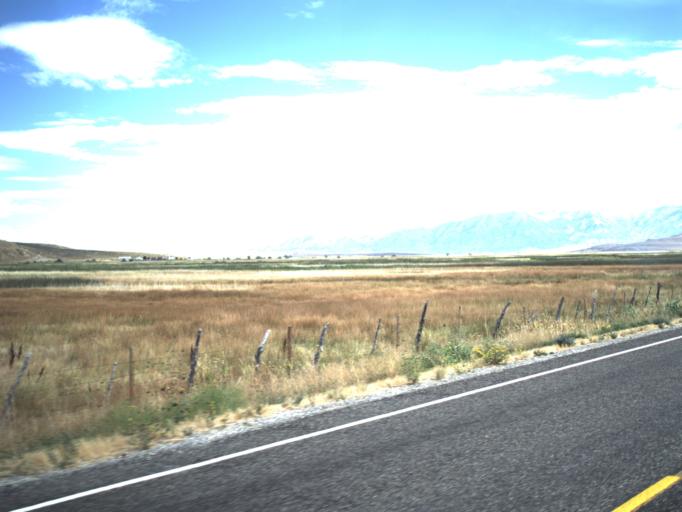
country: US
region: Utah
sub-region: Box Elder County
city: Tremonton
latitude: 41.6123
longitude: -112.3625
